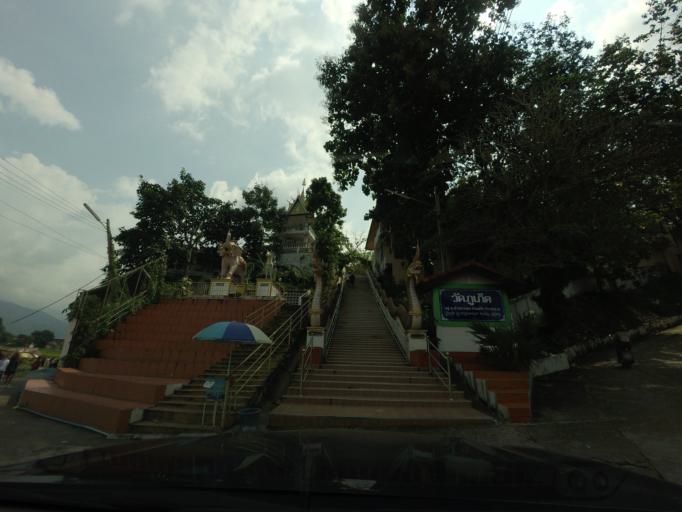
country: TH
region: Nan
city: Pua
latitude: 19.1658
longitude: 100.9342
